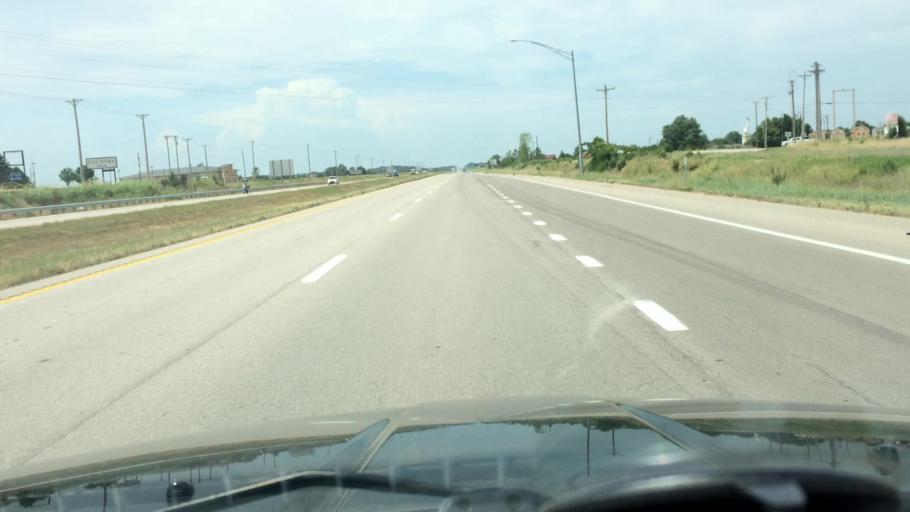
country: US
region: Missouri
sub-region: Polk County
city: Bolivar
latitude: 37.5964
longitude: -93.4351
